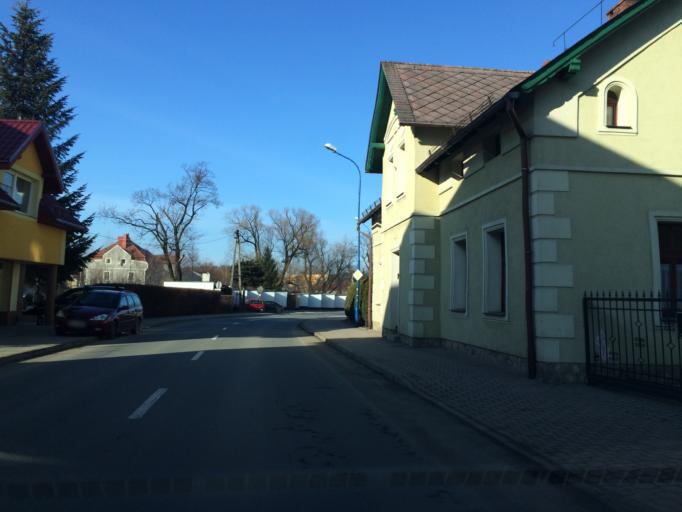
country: PL
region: Lower Silesian Voivodeship
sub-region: Powiat klodzki
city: Stronie Slaskie
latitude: 50.2968
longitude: 16.8743
